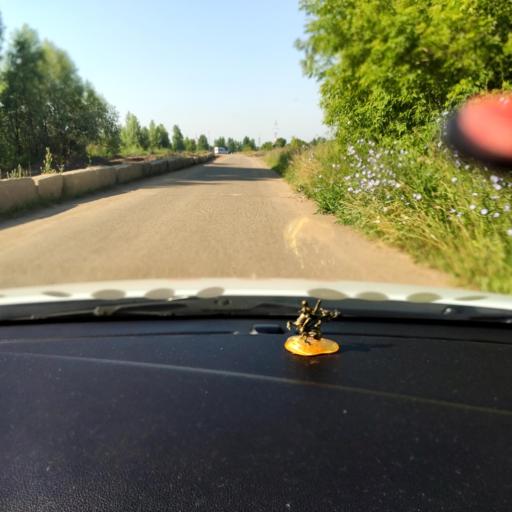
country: RU
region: Tatarstan
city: Stolbishchi
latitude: 55.6971
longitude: 49.2225
